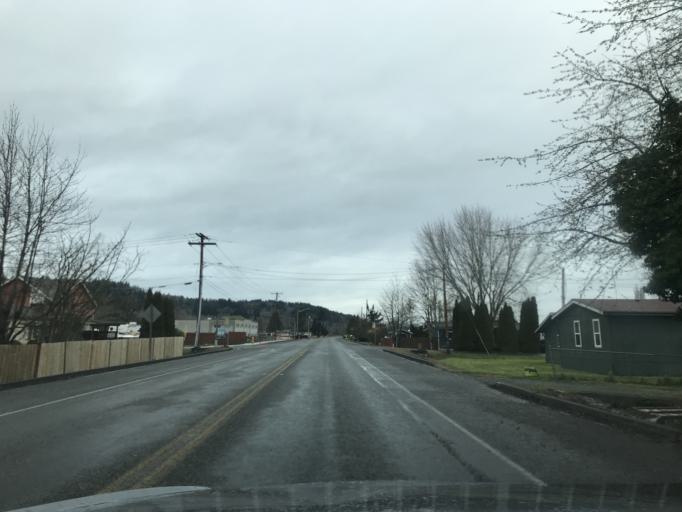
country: US
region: Washington
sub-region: King County
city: Algona
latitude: 47.2882
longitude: -122.2550
